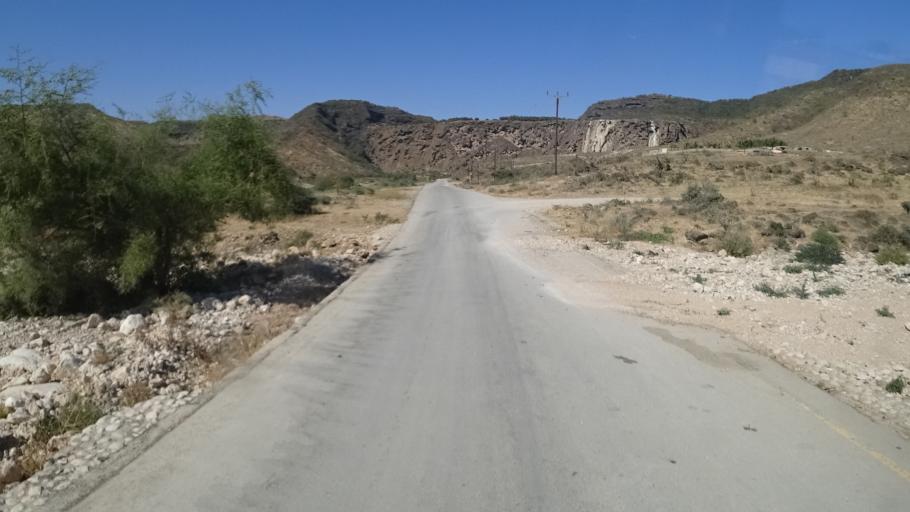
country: OM
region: Zufar
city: Salalah
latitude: 17.0674
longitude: 54.4316
